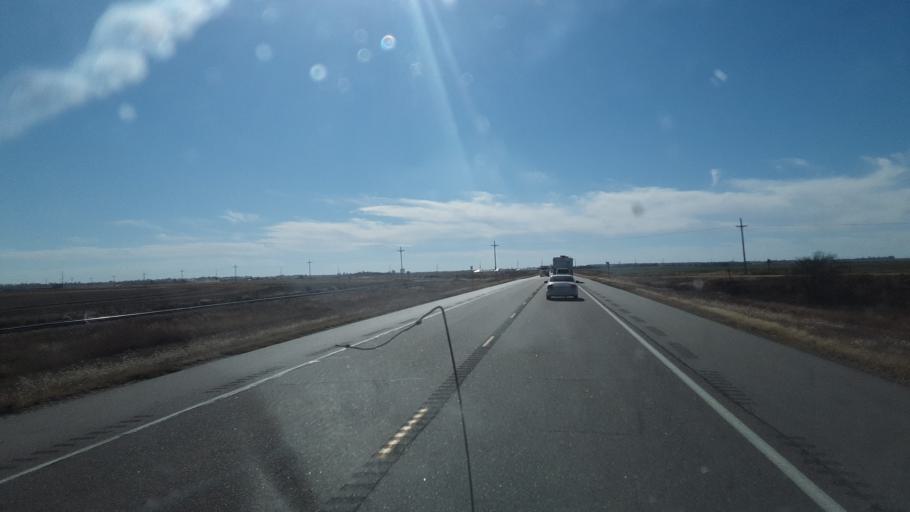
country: US
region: Kansas
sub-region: Pawnee County
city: Larned
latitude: 38.2249
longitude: -99.0392
